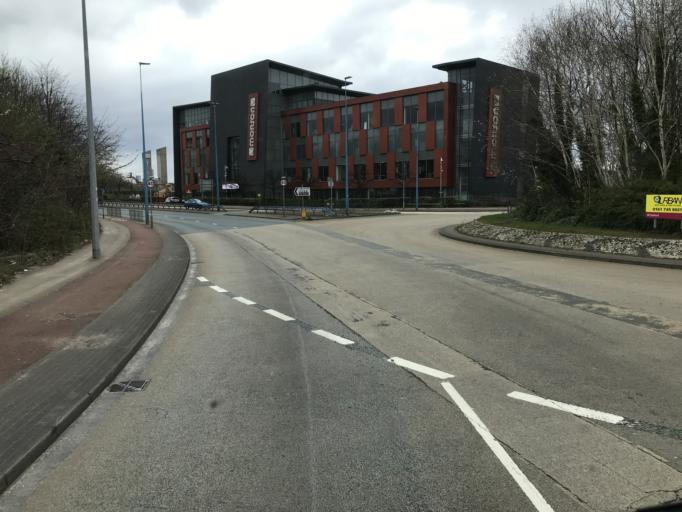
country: GB
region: England
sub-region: City and Borough of Salford
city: Eccles
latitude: 53.4812
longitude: -2.3301
